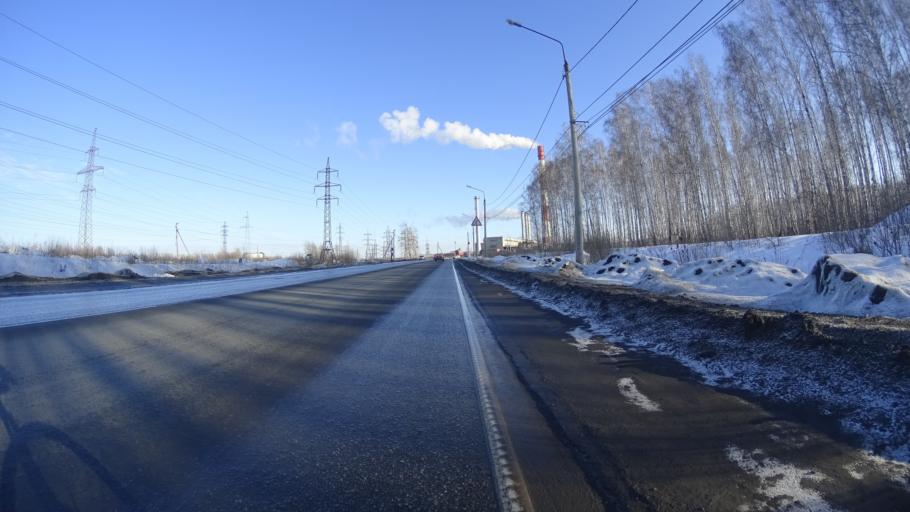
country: RU
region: Chelyabinsk
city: Roshchino
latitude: 55.2100
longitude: 61.3142
